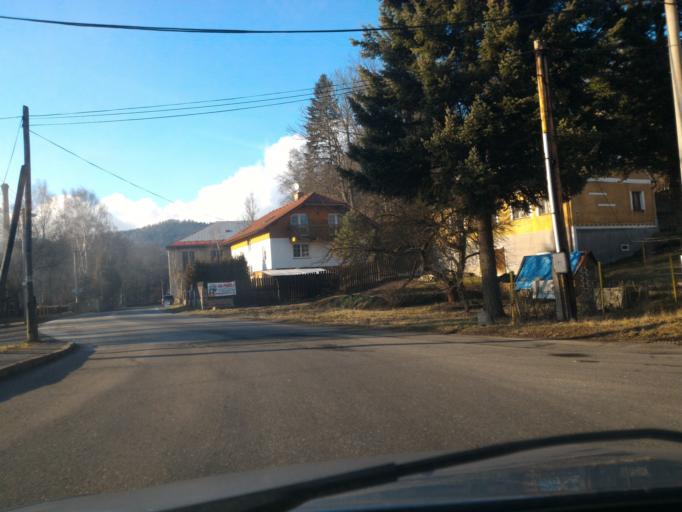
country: CZ
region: Liberecky
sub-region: Okres Jablonec nad Nisou
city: Tanvald
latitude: 50.7375
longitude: 15.2767
